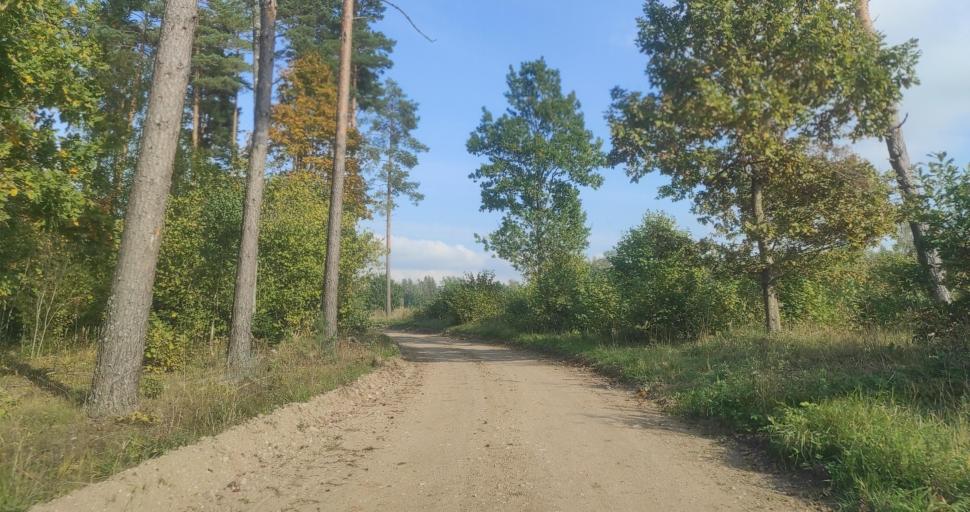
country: LV
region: Alsunga
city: Alsunga
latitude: 57.0041
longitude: 21.6083
